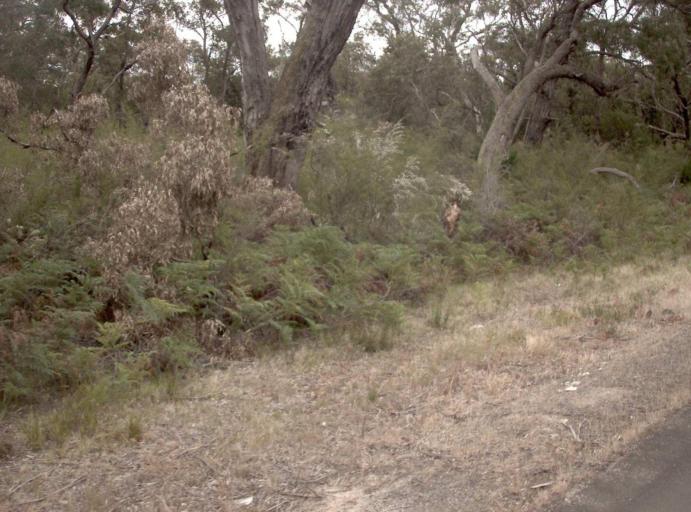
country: AU
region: Victoria
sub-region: Wellington
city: Sale
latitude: -38.2654
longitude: 147.0356
